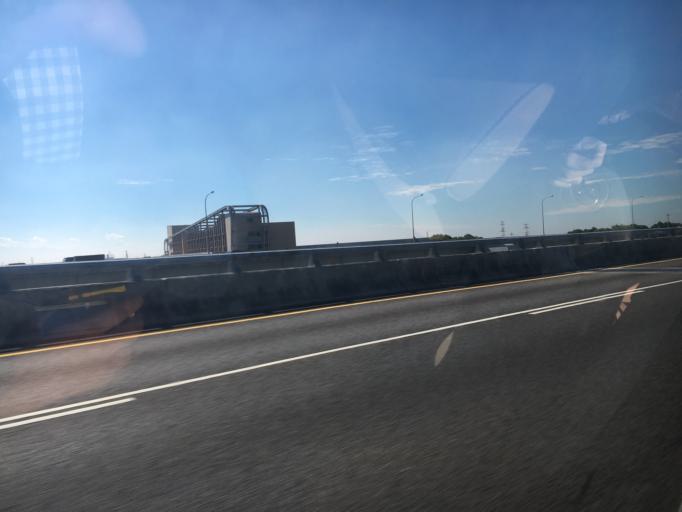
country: TW
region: Taiwan
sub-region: Taoyuan
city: Taoyuan
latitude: 25.0658
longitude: 121.3536
